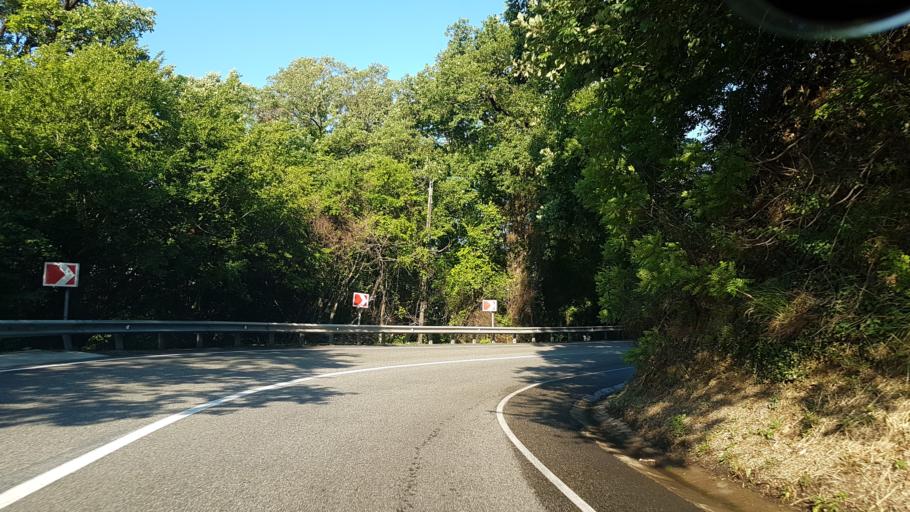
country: RU
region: Krasnodarskiy
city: Vardane
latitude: 43.8150
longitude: 39.4428
